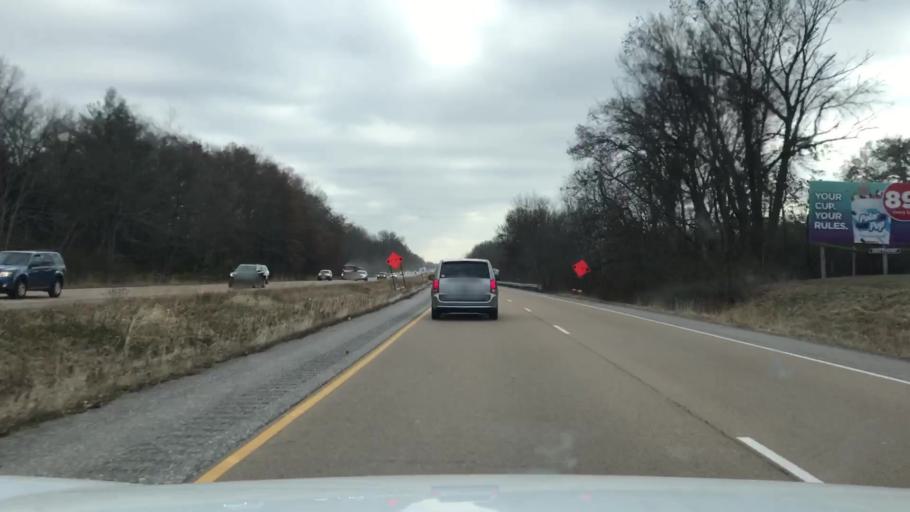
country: US
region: Illinois
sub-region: Saint Clair County
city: Belleville
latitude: 38.5122
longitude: -90.0169
